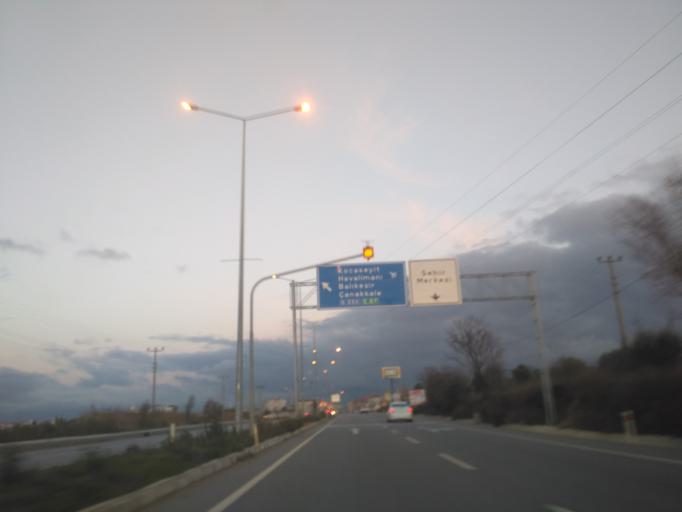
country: TR
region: Balikesir
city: Burhaniye
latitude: 39.4881
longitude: 26.9551
